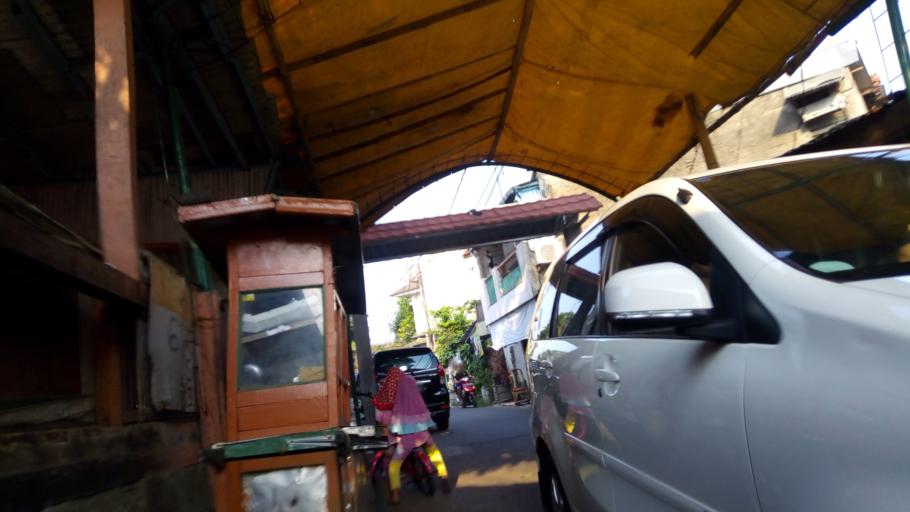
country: ID
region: Jakarta Raya
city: Jakarta
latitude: -6.2059
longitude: 106.8446
